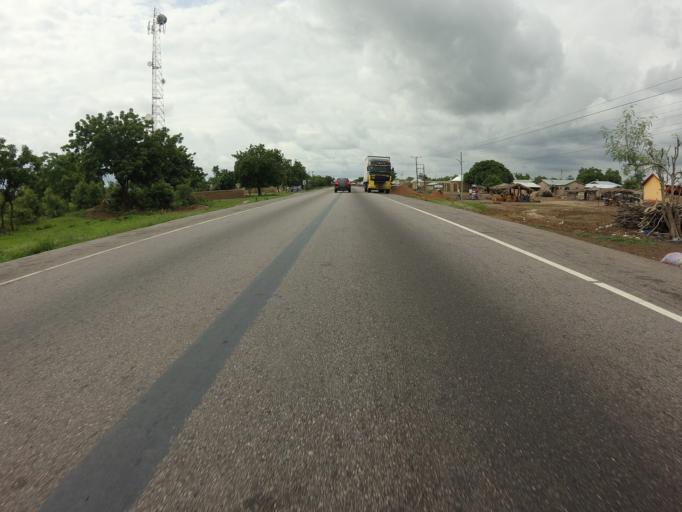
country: GH
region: Northern
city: Tamale
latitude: 8.9819
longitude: -1.3573
